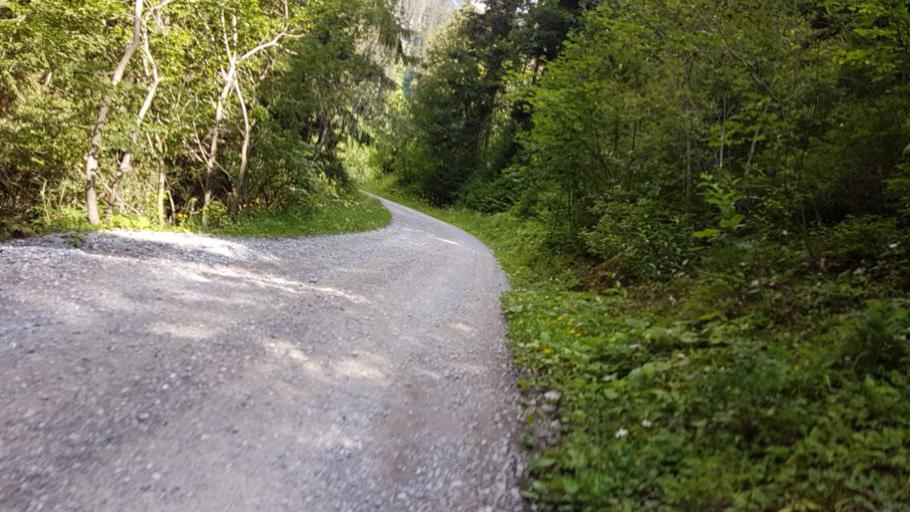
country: CH
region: Bern
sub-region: Obersimmental-Saanen District
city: Boltigen
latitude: 46.6841
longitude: 7.4492
